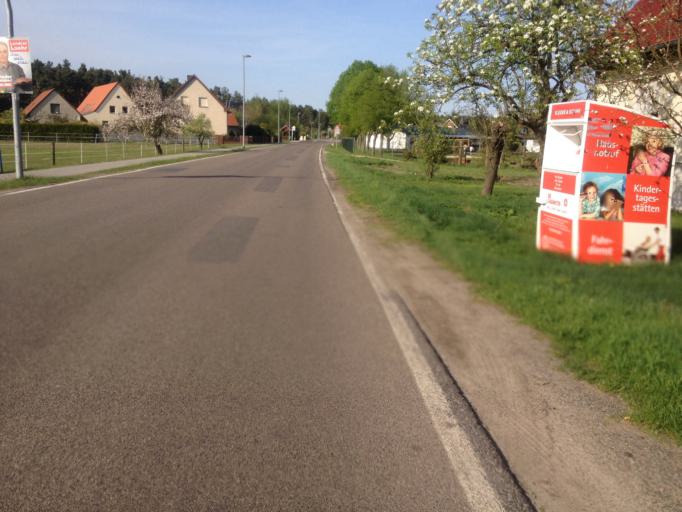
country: DE
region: Brandenburg
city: Briesen
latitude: 51.8542
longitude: 14.2492
